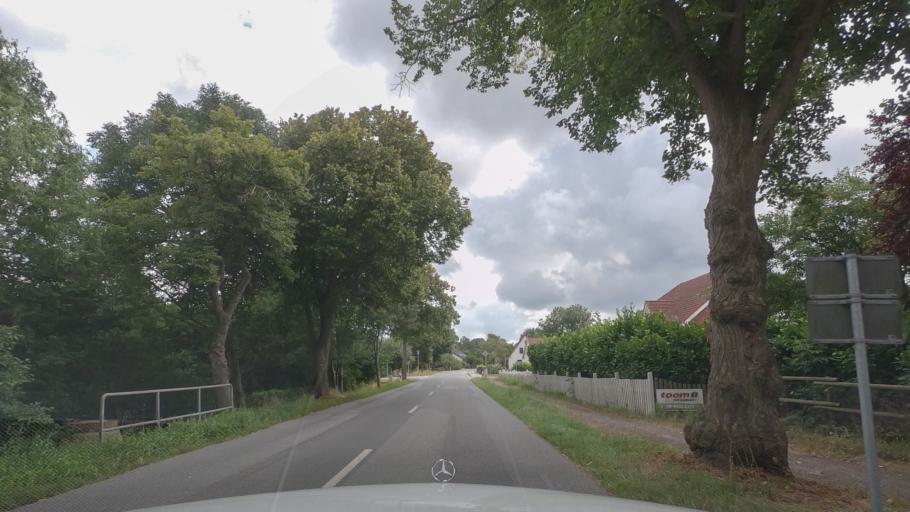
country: DE
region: Lower Saxony
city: Uthlede
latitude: 53.3115
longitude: 8.5741
